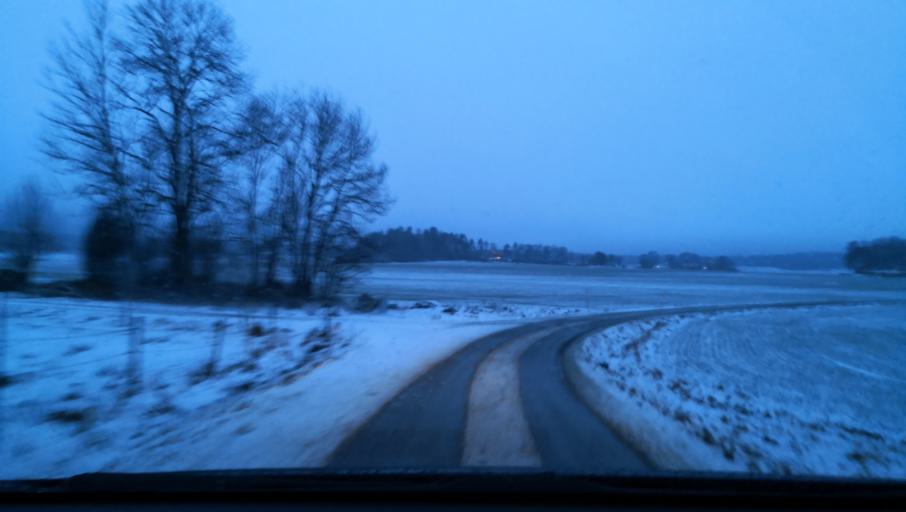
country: SE
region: Soedermanland
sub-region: Eskilstuna Kommun
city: Kvicksund
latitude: 59.3716
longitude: 16.2928
